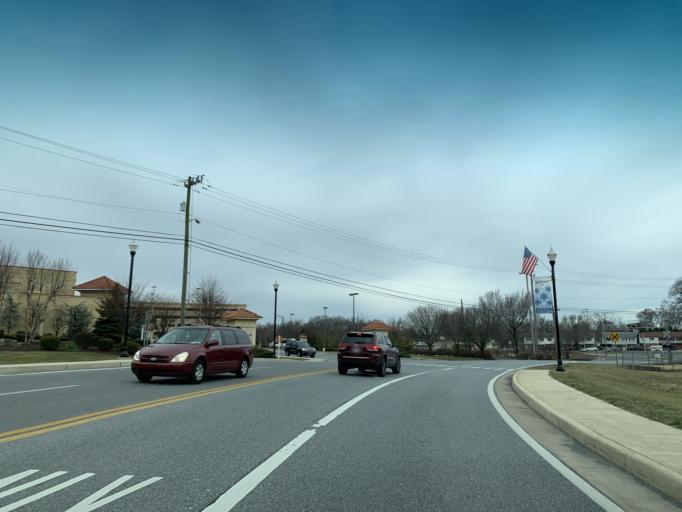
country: US
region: West Virginia
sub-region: Jefferson County
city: Ranson
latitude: 39.2986
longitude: -77.8518
